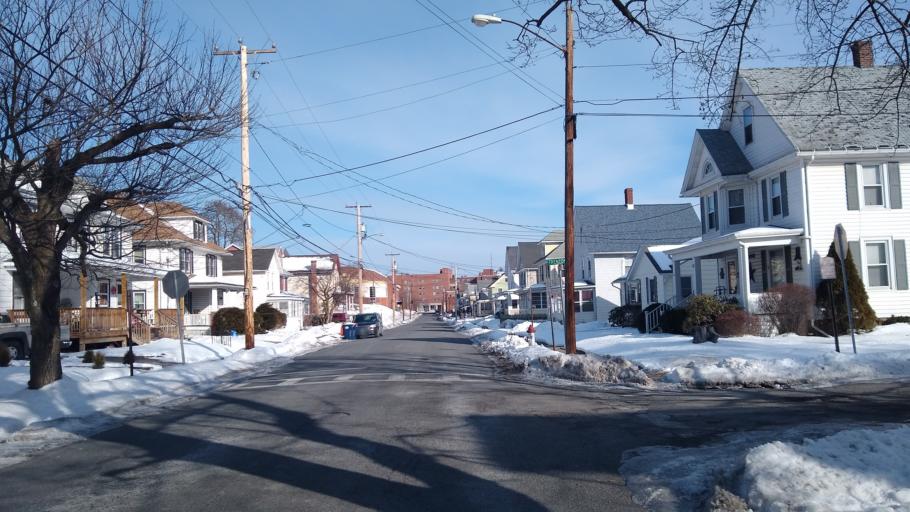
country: US
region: New York
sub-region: Ulster County
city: Kingston
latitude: 41.9231
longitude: -73.9965
